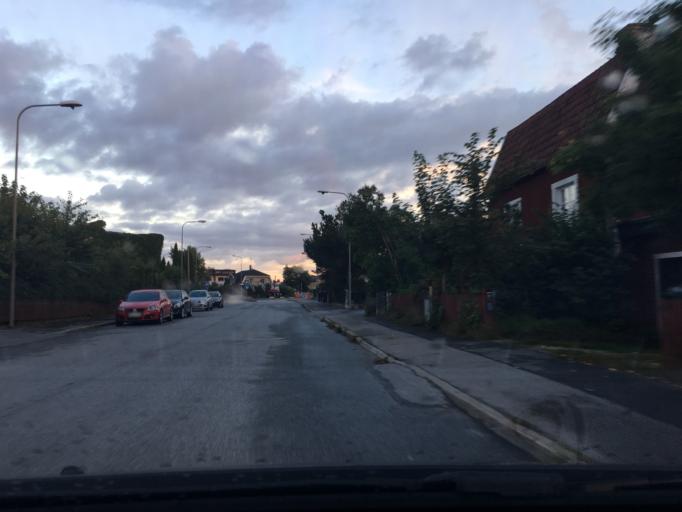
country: SE
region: Stockholm
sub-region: Jarfalla Kommun
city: Jakobsberg
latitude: 59.3758
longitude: 17.8772
